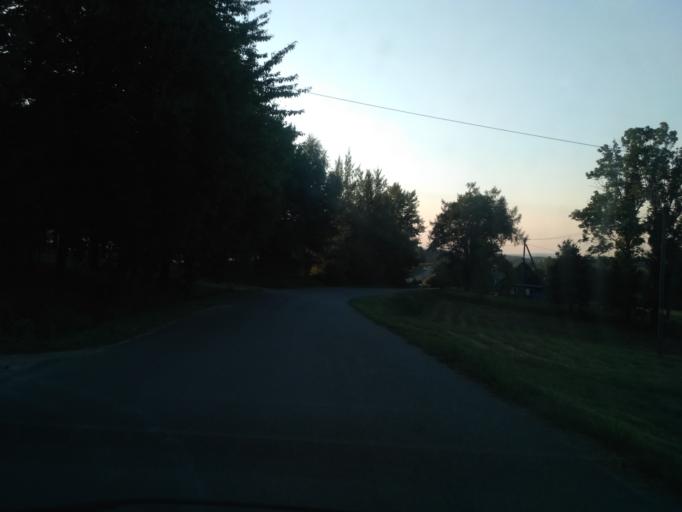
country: PL
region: Subcarpathian Voivodeship
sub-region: Powiat strzyzowski
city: Wysoka Strzyzowska
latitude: 49.8101
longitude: 21.7444
